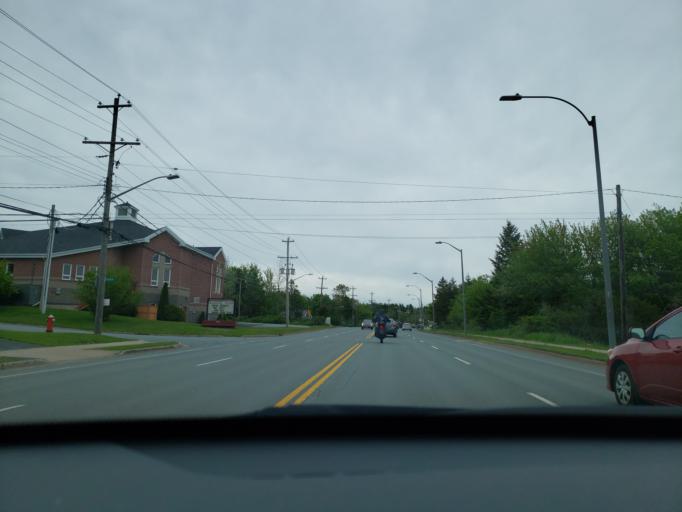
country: CA
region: Nova Scotia
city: Cole Harbour
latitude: 44.6857
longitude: -63.5234
